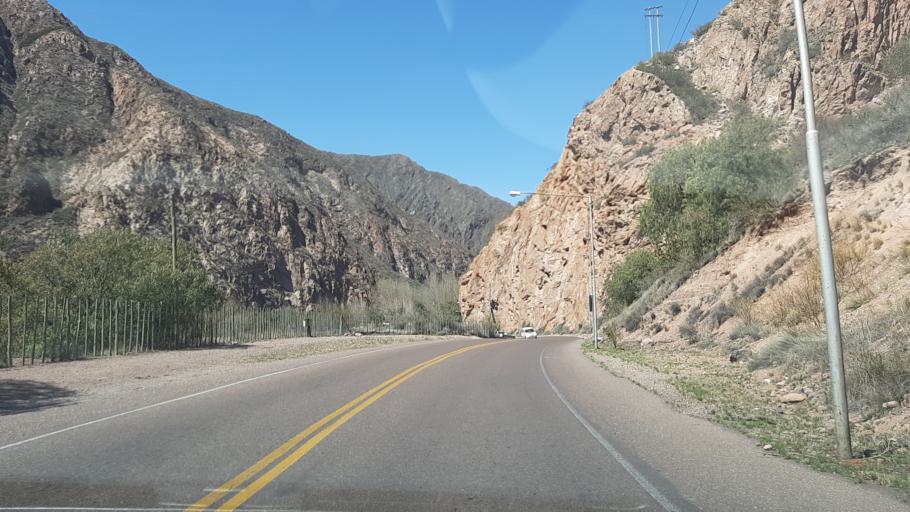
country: AR
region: Mendoza
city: Lujan de Cuyo
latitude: -33.0295
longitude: -69.1127
